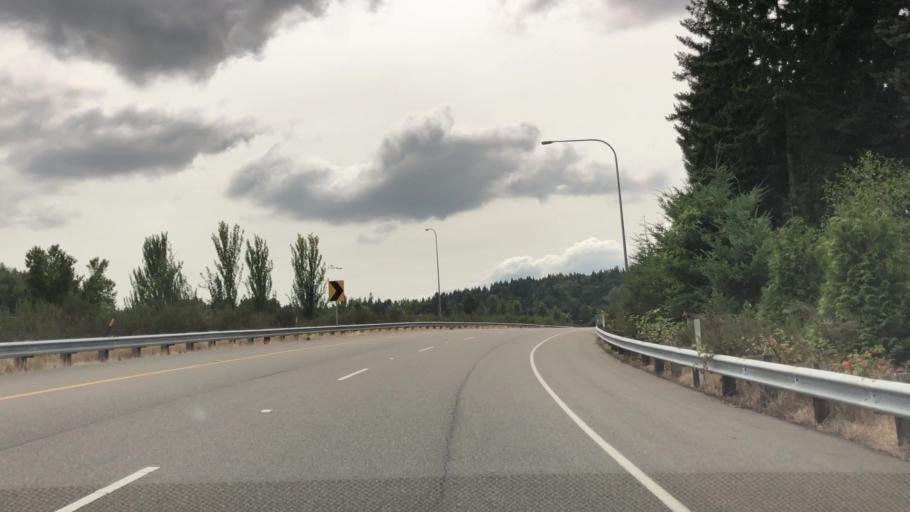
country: US
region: Washington
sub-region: King County
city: Bothell
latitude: 47.7598
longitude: -122.1852
